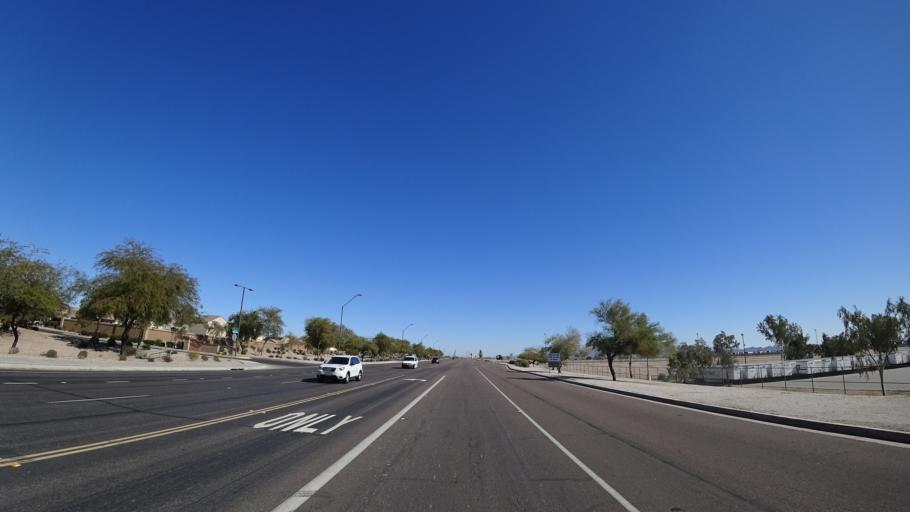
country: US
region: Arizona
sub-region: Maricopa County
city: Buckeye
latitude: 33.3921
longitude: -112.5613
